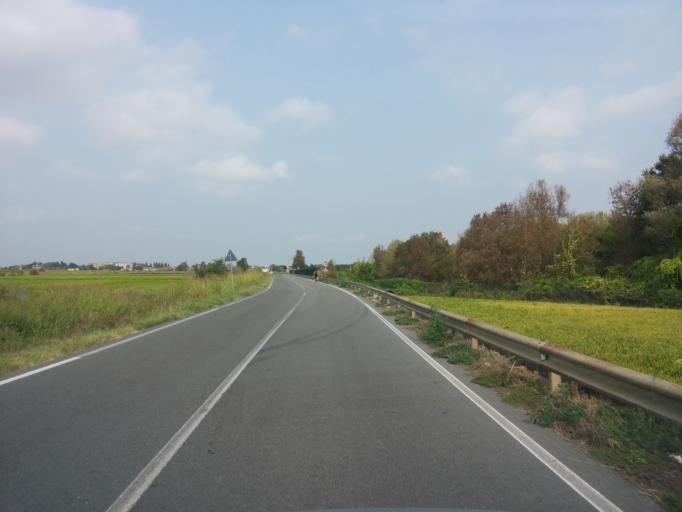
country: IT
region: Piedmont
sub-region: Provincia di Vercelli
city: Prarolo
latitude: 45.2978
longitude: 8.4661
